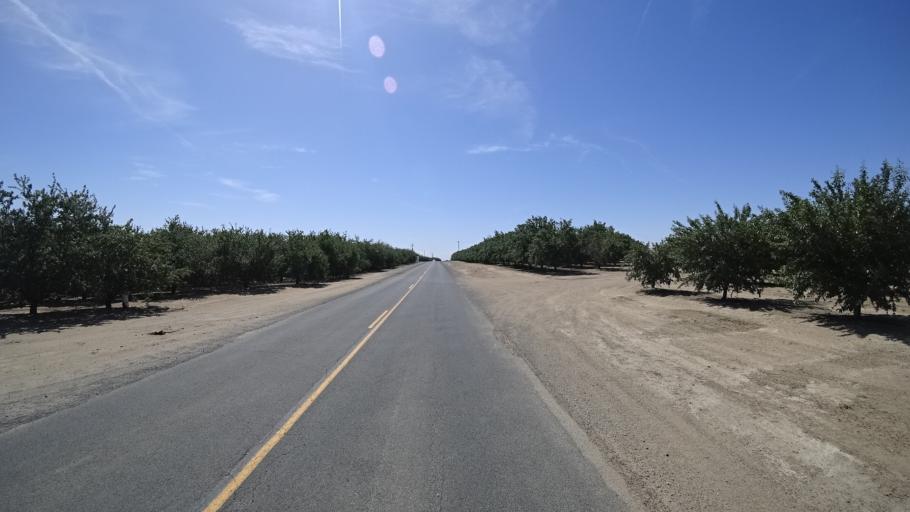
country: US
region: California
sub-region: Kings County
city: Kettleman City
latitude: 35.9815
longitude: -119.9503
